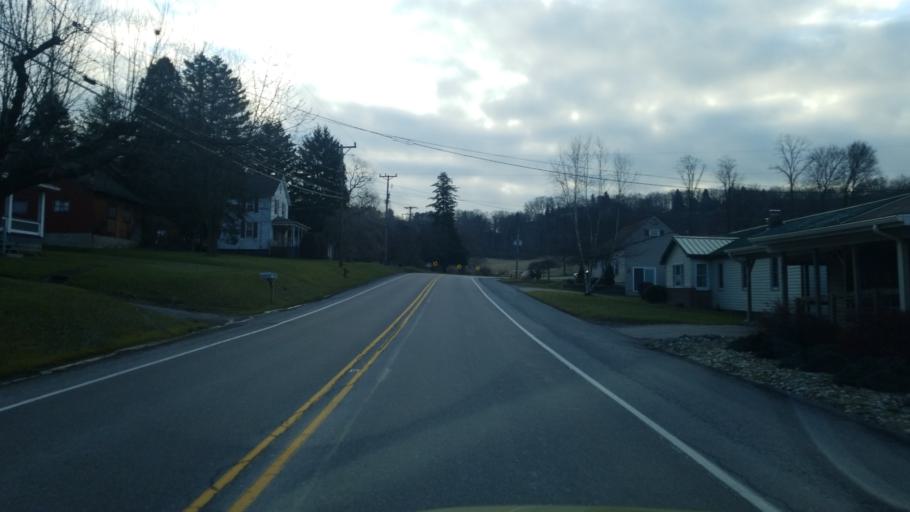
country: US
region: Pennsylvania
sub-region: Clearfield County
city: Clearfield
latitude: 41.0073
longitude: -78.4290
